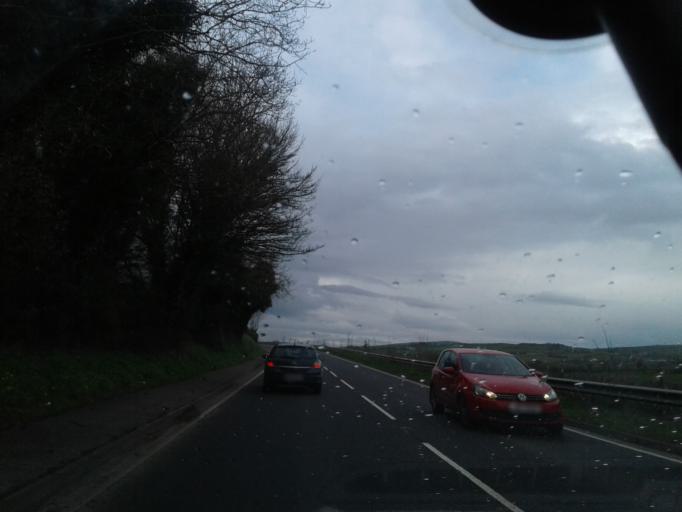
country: GB
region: Northern Ireland
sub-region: Strabane District
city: Sion Mills
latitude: 54.7710
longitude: -7.4665
